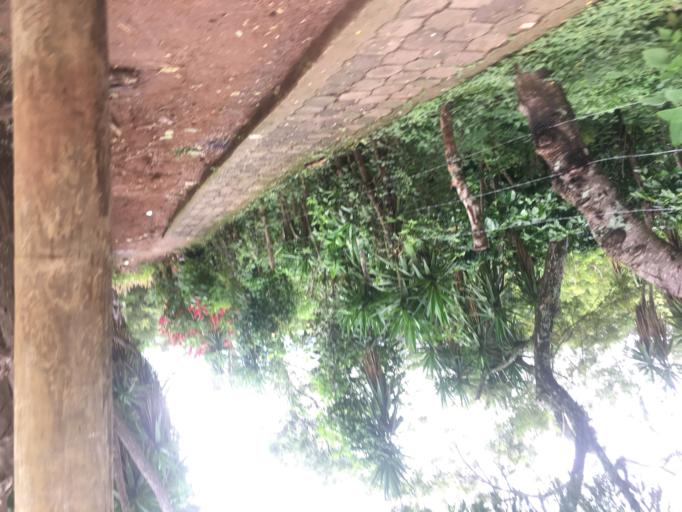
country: GT
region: Escuintla
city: San Vicente Pacaya
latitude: 14.3238
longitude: -90.5620
